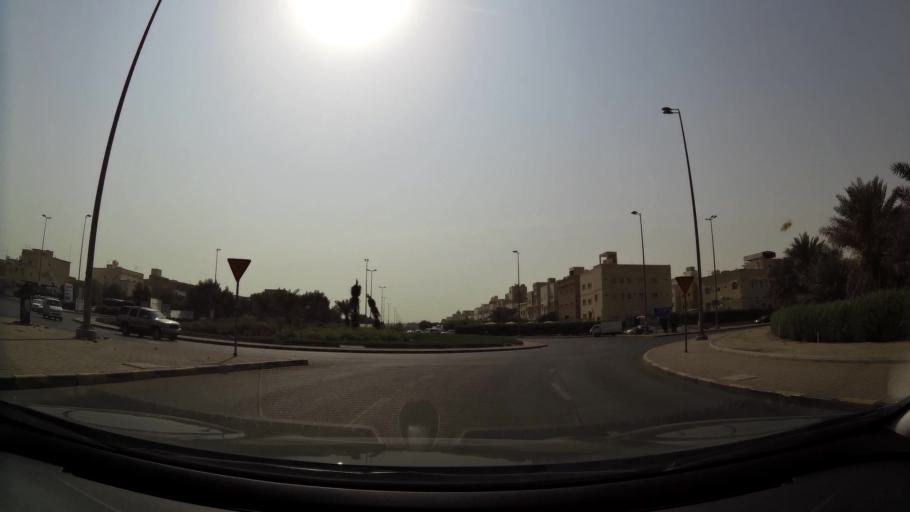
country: KW
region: Al Asimah
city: Ar Rabiyah
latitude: 29.2816
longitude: 47.8866
